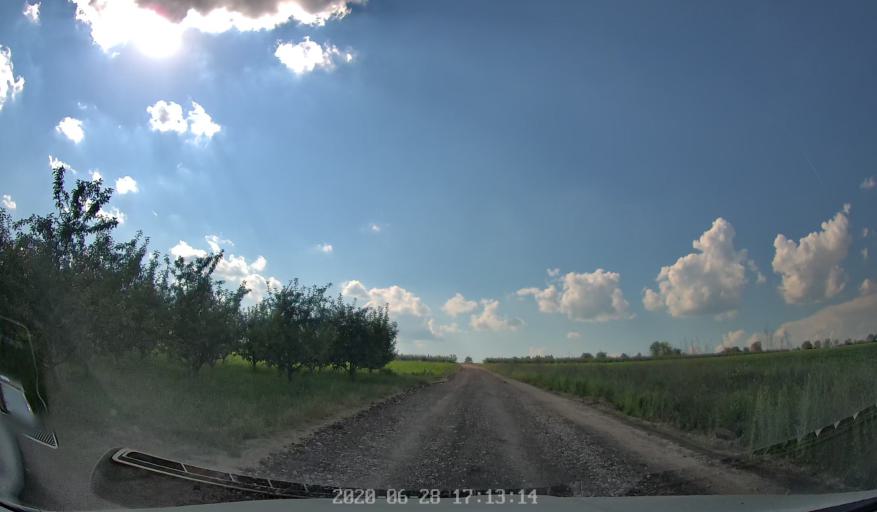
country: MD
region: Chisinau
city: Vatra
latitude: 46.9904
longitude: 28.6978
